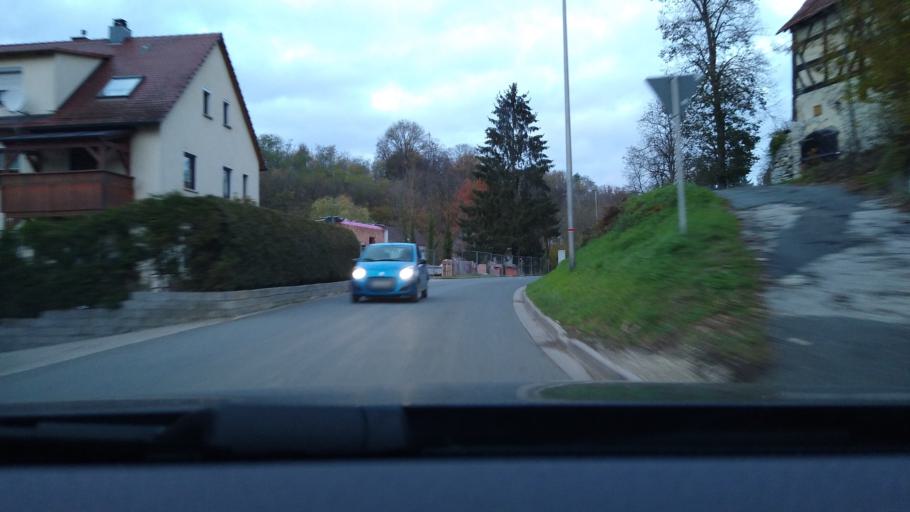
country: DE
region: Bavaria
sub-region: Upper Franconia
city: Grafenberg
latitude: 49.6486
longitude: 11.2489
